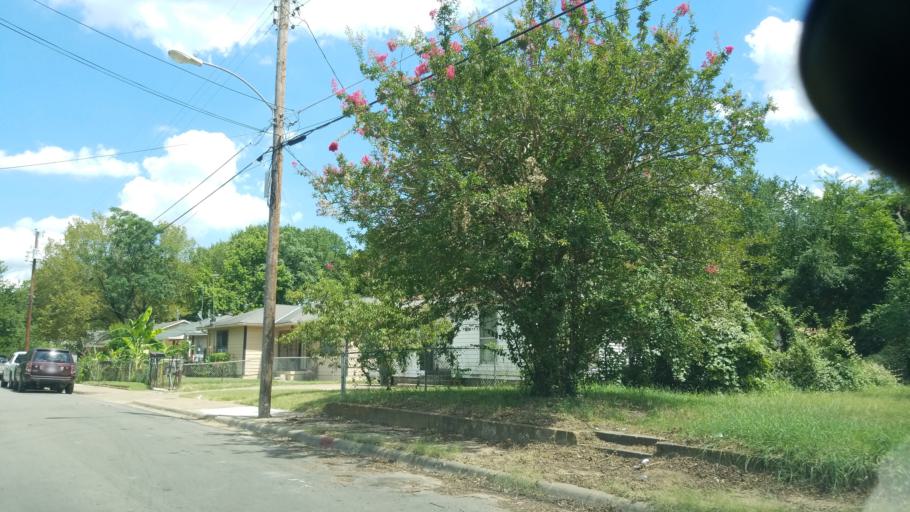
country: US
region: Texas
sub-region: Dallas County
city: Dallas
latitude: 32.7515
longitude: -96.7499
